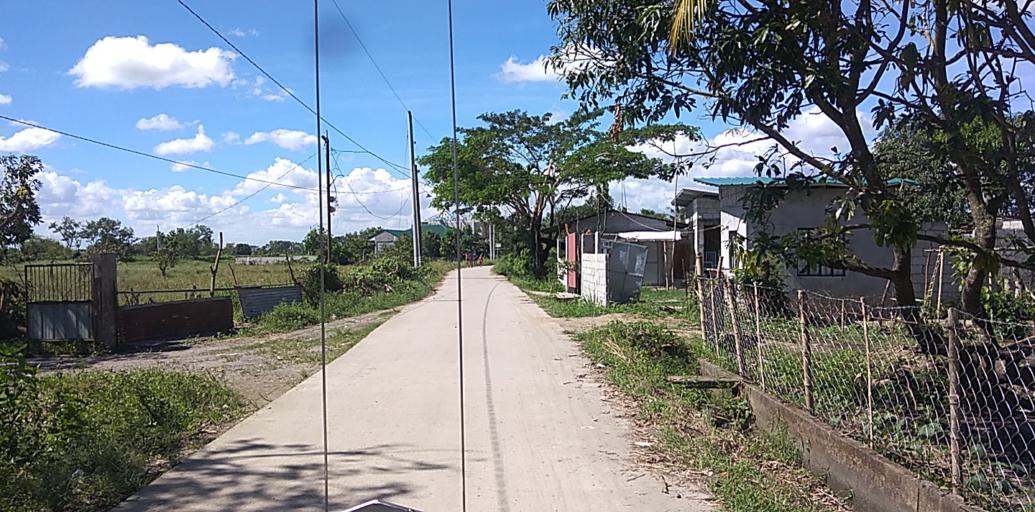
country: PH
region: Central Luzon
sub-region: Province of Pampanga
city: Arayat
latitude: 15.1273
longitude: 120.7838
